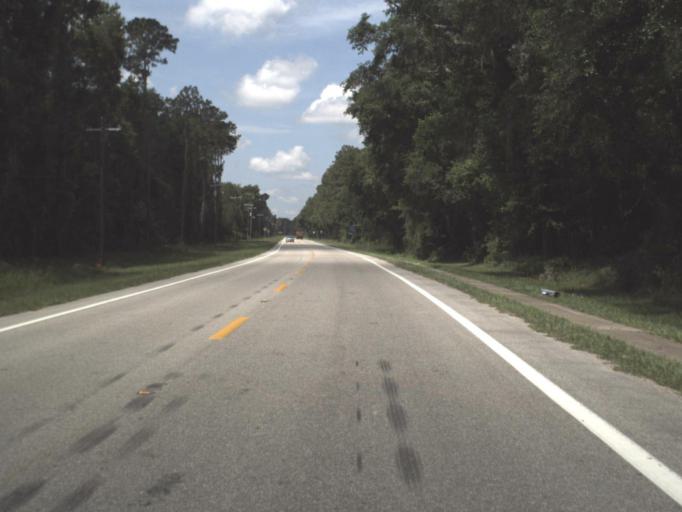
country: US
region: Florida
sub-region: Levy County
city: Bronson
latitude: 29.4459
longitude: -82.6448
